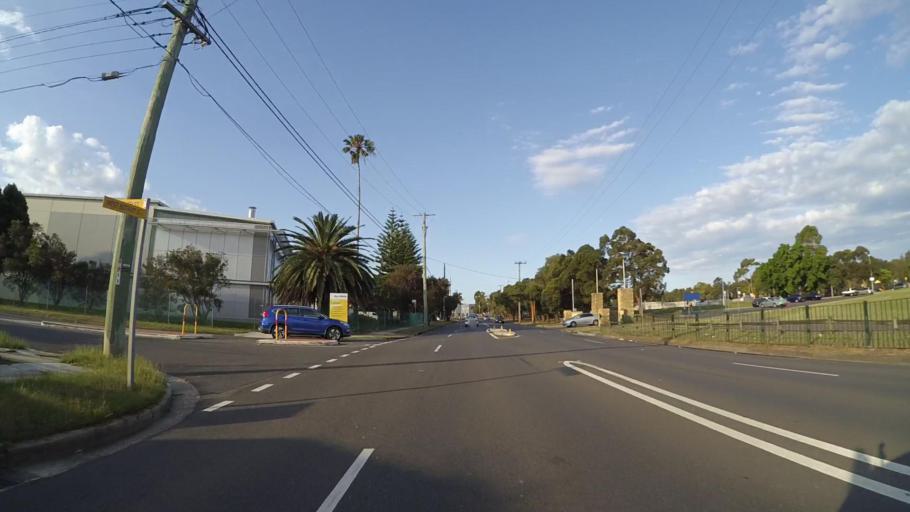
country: AU
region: New South Wales
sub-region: Rockdale
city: Brighton-Le-Sands
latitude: -33.9628
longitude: 151.1438
